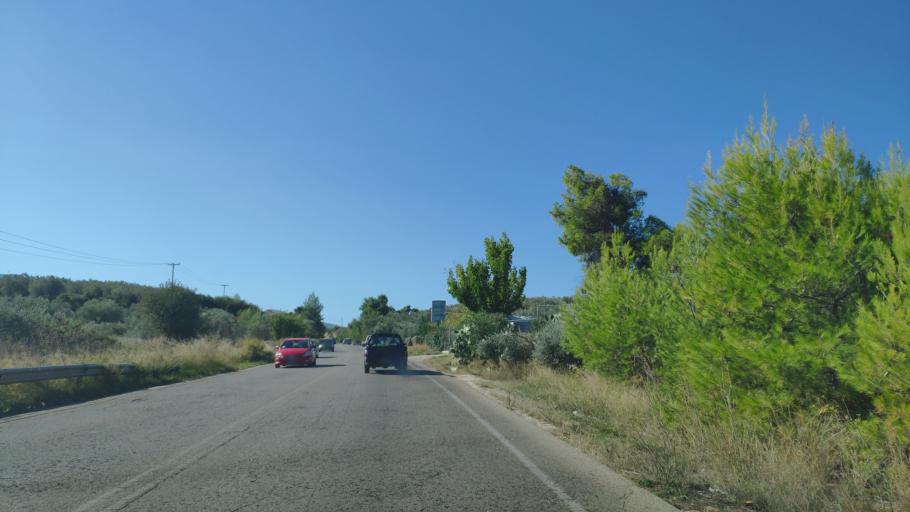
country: GR
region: Peloponnese
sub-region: Nomos Korinthias
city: Khiliomodhi
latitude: 37.8221
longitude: 22.8795
